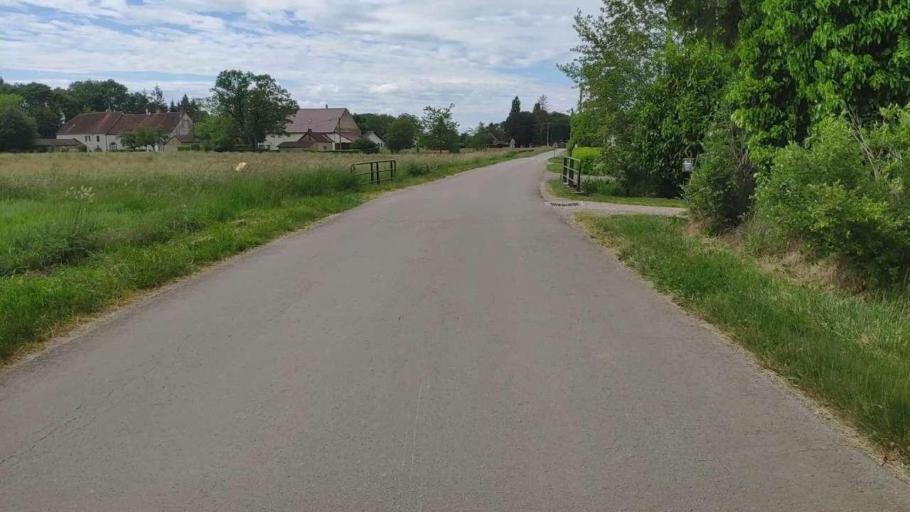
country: FR
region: Franche-Comte
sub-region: Departement du Jura
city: Bletterans
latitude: 46.7389
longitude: 5.5033
